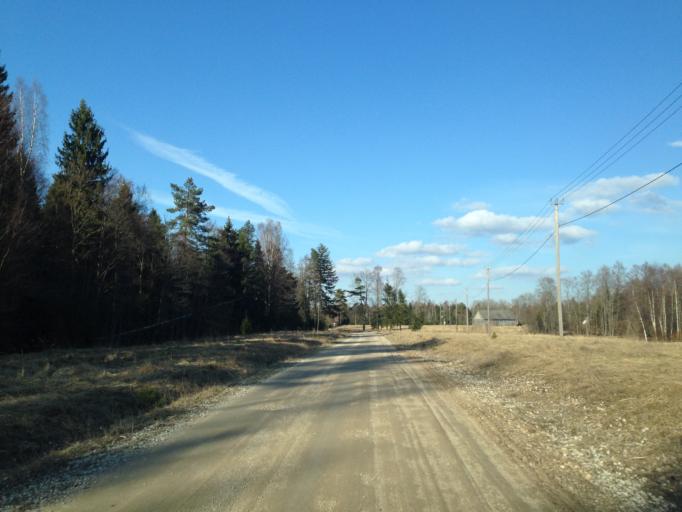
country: EE
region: Harju
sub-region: Nissi vald
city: Turba
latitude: 59.1361
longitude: 24.1741
